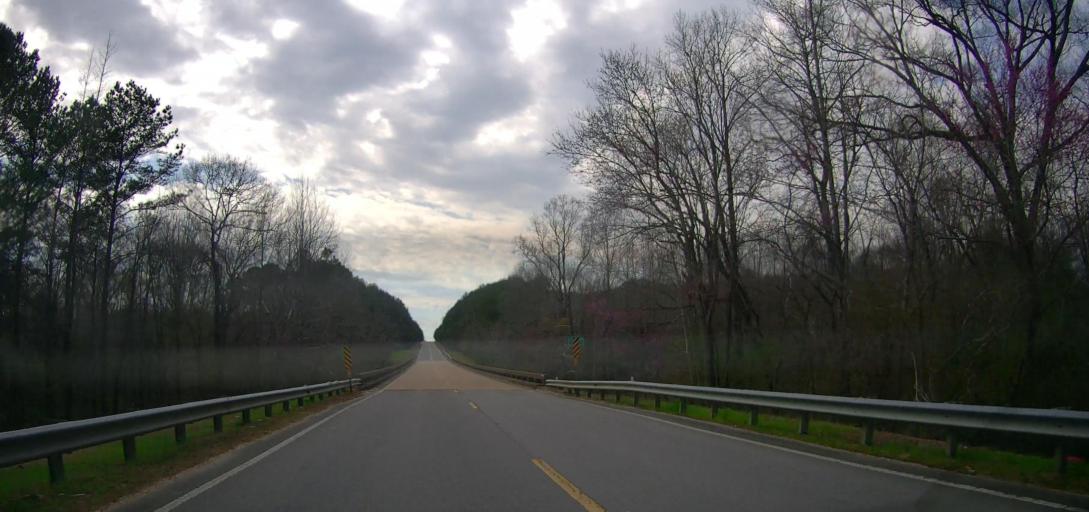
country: US
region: Alabama
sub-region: Marion County
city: Winfield
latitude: 33.9337
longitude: -87.7357
